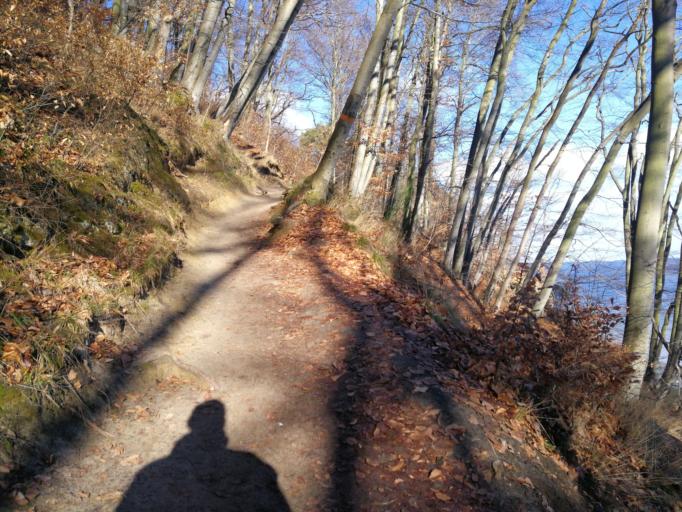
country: PL
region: Pomeranian Voivodeship
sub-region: Sopot
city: Sopot
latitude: 54.4839
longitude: 18.5659
